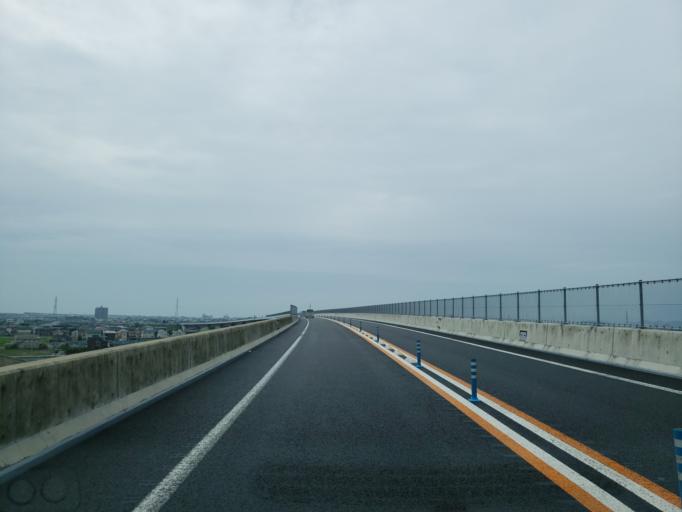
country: JP
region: Tokushima
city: Tokushima-shi
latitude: 34.1270
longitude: 134.5655
